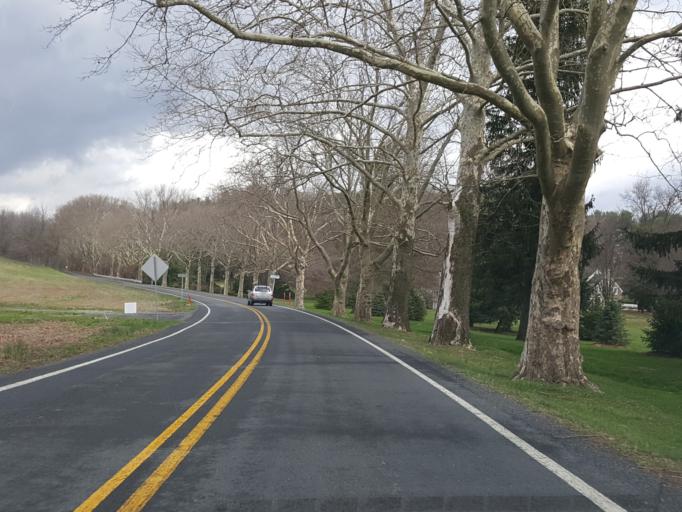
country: US
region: Pennsylvania
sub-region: Berks County
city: Robesonia
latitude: 40.3562
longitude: -76.1422
